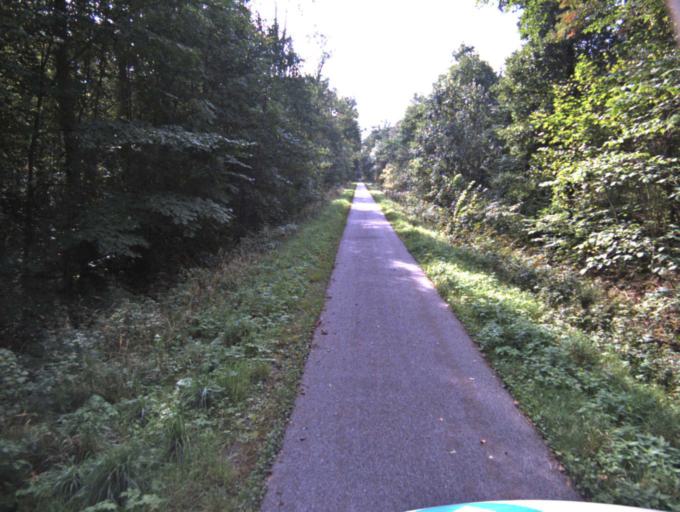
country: SE
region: Vaestra Goetaland
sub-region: Tranemo Kommun
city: Limmared
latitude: 57.6511
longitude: 13.3610
